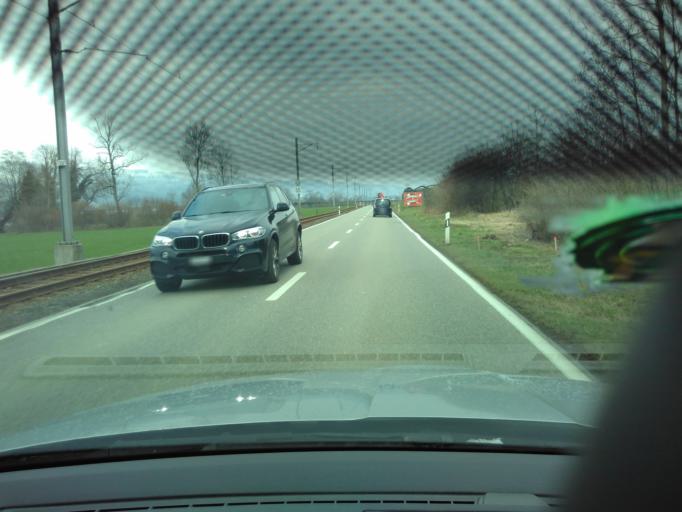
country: CH
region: Lucerne
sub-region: Hochdorf District
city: Hitzkirch
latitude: 47.1997
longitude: 8.2733
